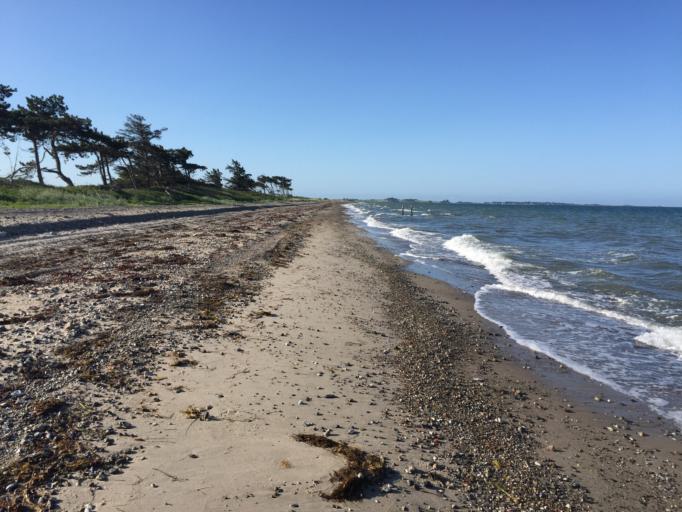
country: DK
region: Zealand
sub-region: Slagelse Kommune
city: Korsor
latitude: 55.2114
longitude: 11.1726
